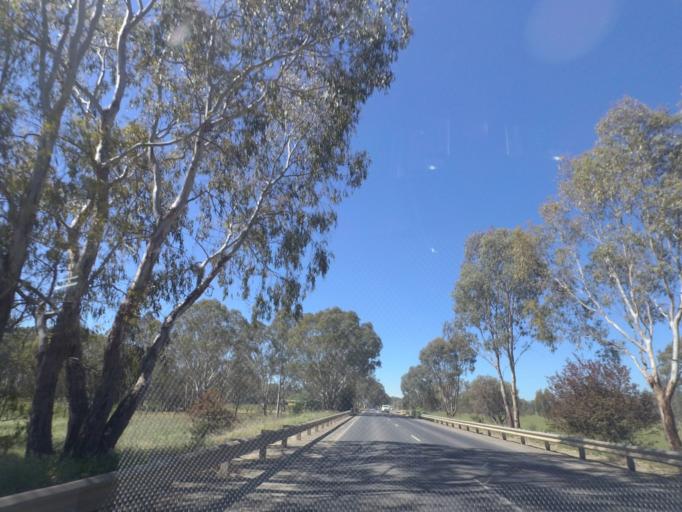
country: AU
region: Victoria
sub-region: Murrindindi
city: Kinglake West
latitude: -37.0246
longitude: 145.1124
